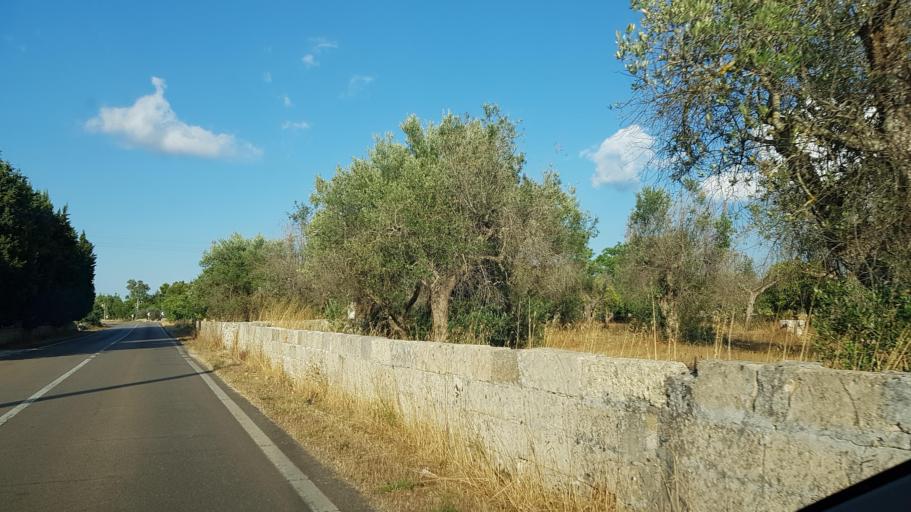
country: IT
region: Apulia
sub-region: Provincia di Lecce
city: Montesano Salentino
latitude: 39.9758
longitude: 18.3326
